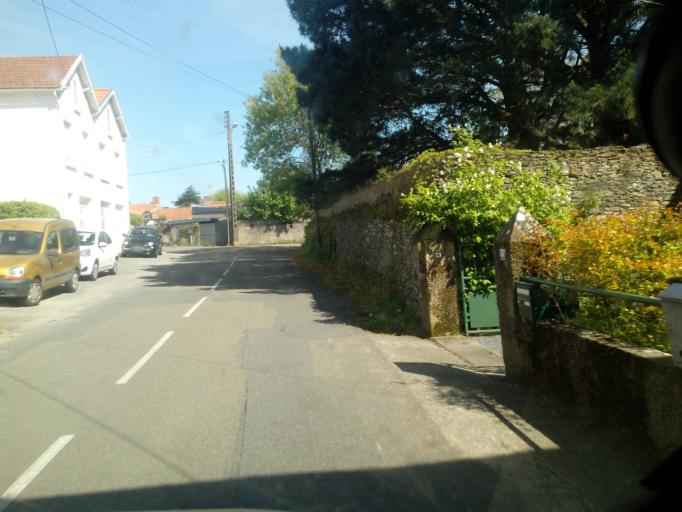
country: FR
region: Pays de la Loire
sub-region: Departement de la Loire-Atlantique
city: Pornic
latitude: 47.1083
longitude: -2.0915
